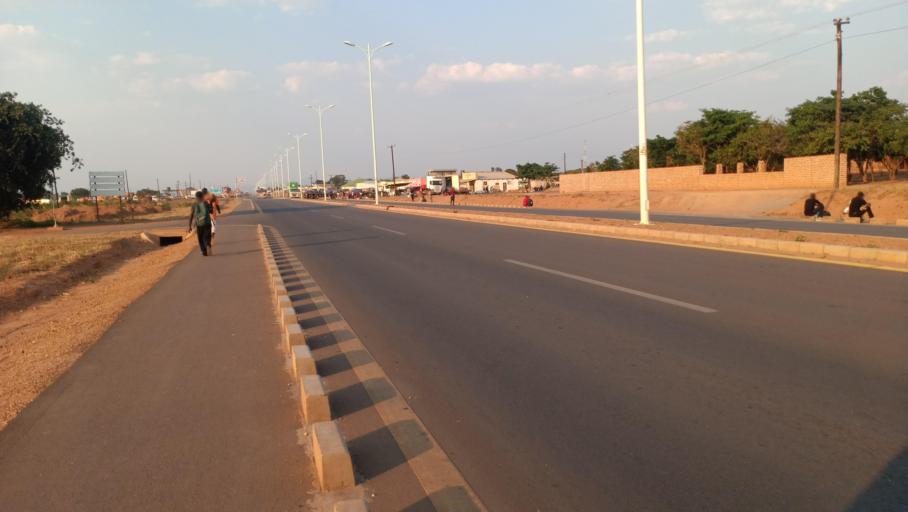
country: ZM
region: Northern
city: Mpika
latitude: -11.8473
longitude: 31.4425
